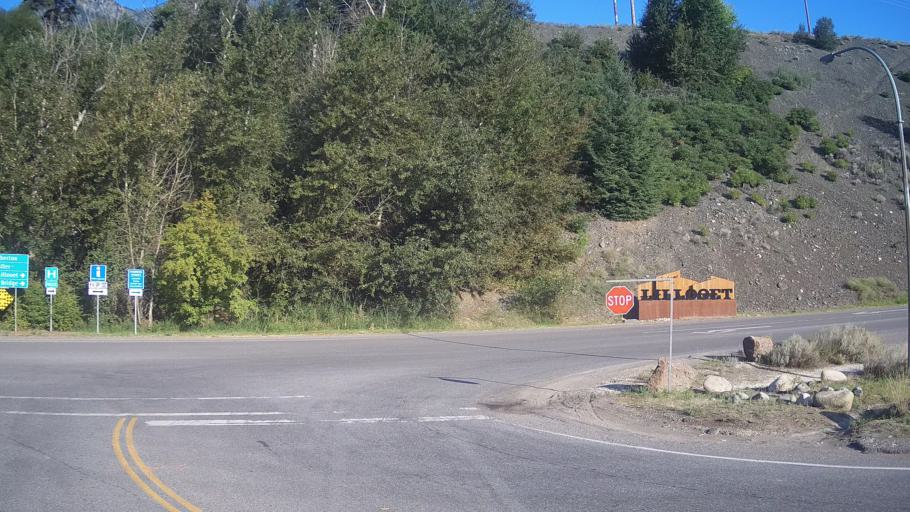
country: CA
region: British Columbia
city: Lillooet
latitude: 50.6805
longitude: -121.9335
